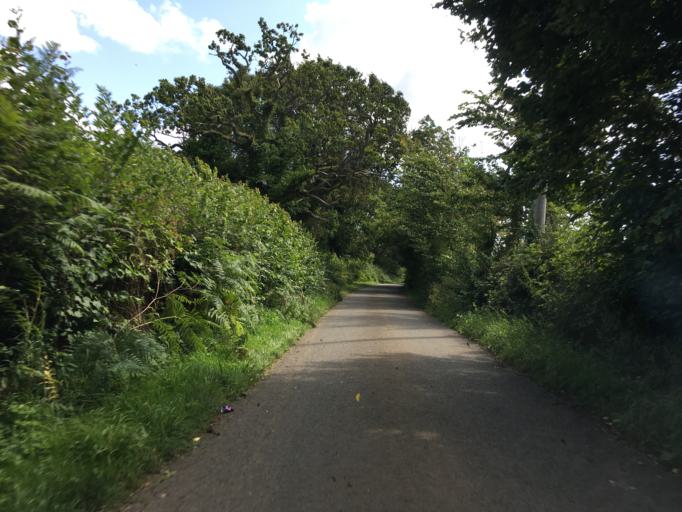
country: GB
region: England
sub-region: Wiltshire
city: Luckington
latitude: 51.6028
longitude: -2.2472
